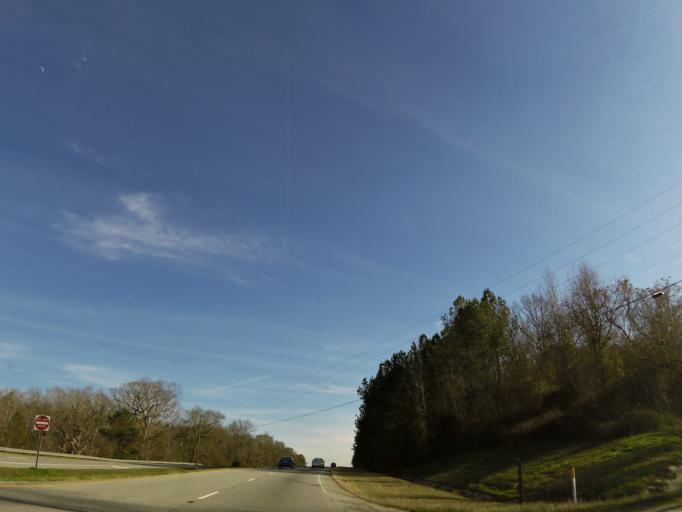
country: US
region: Georgia
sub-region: Chattahoochee County
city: Cusseta
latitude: 32.2585
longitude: -84.7268
